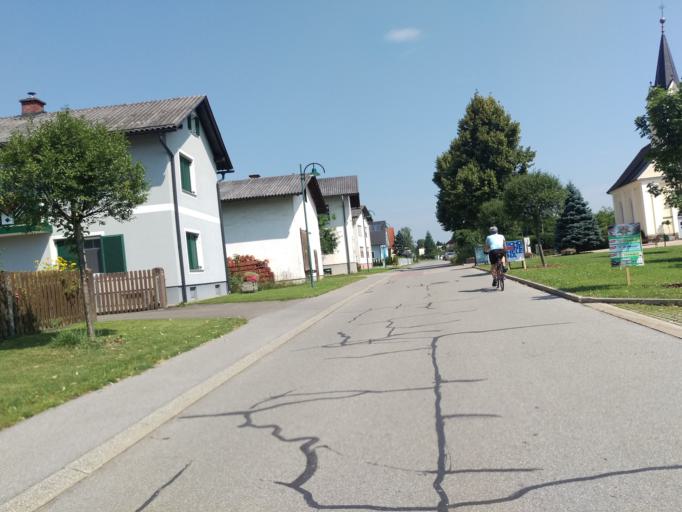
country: AT
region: Styria
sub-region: Politischer Bezirk Graz-Umgebung
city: Werndorf
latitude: 46.9238
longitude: 15.4903
